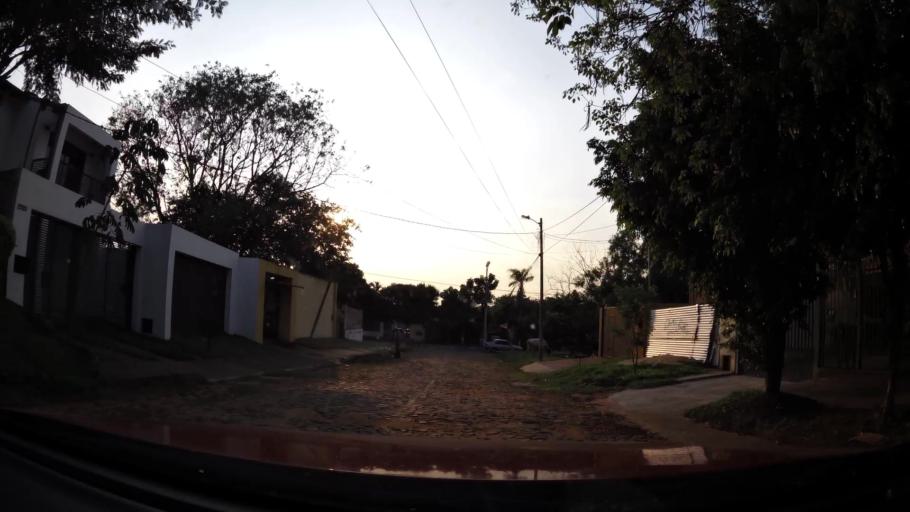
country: PY
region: Central
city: Lambare
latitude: -25.3541
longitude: -57.6035
